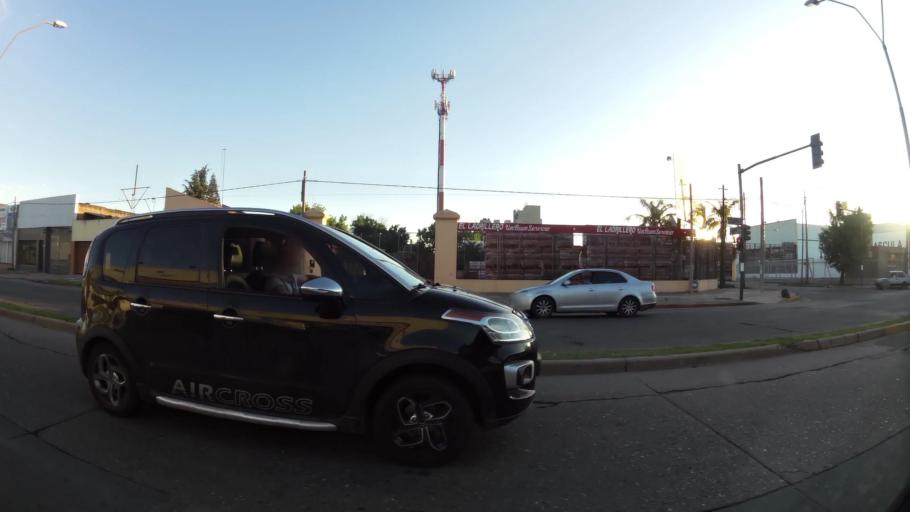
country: AR
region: Santa Fe
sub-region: Departamento de Rosario
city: Rosario
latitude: -32.9617
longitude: -60.6762
